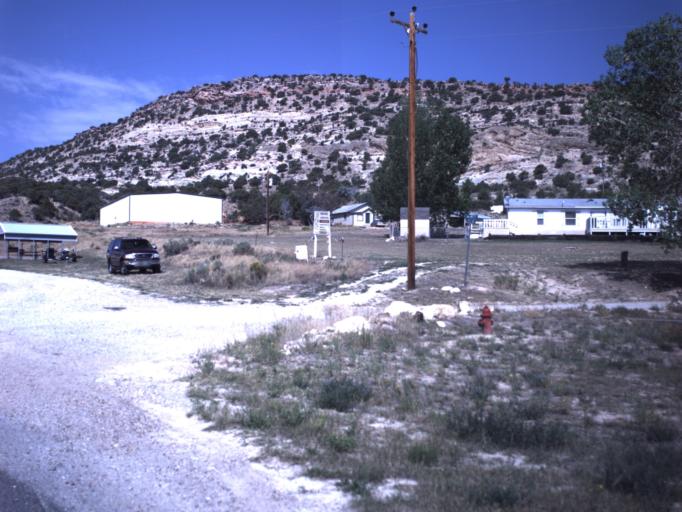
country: US
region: Utah
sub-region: Daggett County
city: Manila
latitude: 40.9880
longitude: -109.7321
